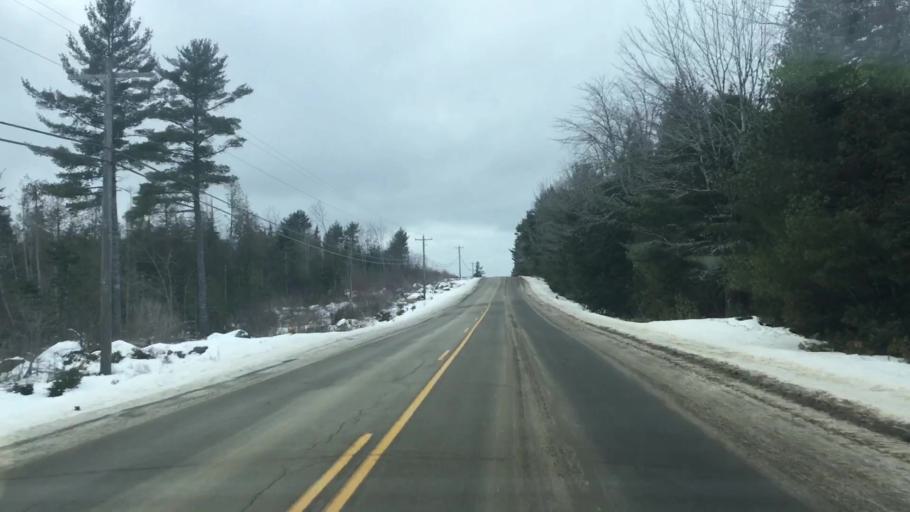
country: US
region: Maine
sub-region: Washington County
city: Calais
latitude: 45.0076
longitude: -67.4080
